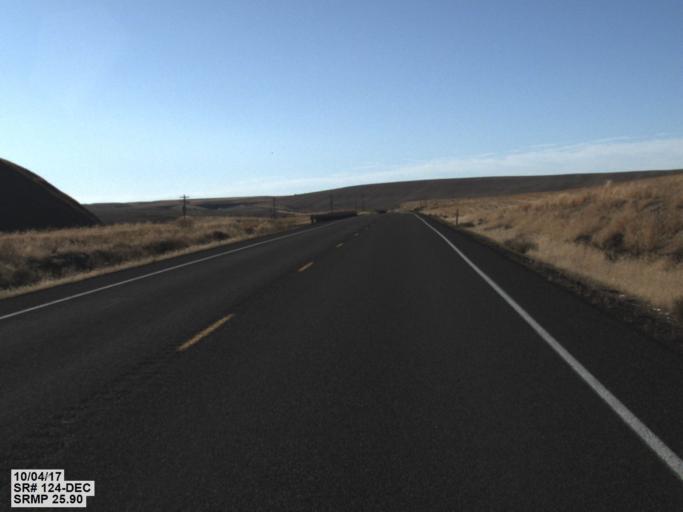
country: US
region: Washington
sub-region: Walla Walla County
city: Garrett
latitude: 46.2907
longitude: -118.5199
